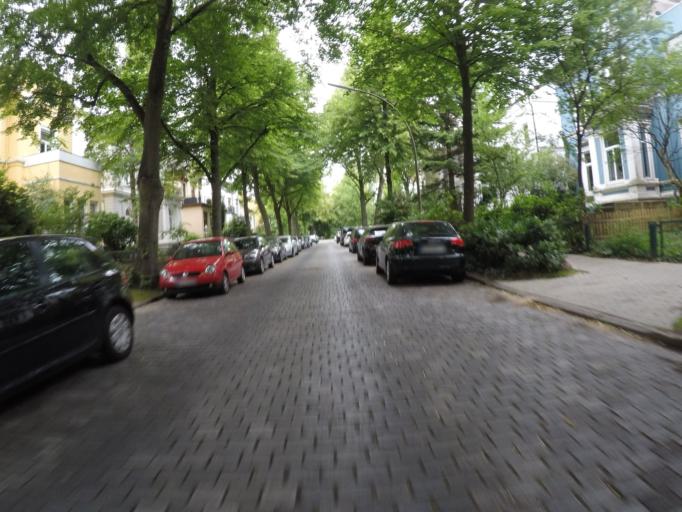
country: DE
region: Hamburg
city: Borgfelde
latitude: 53.5593
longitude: 10.0416
